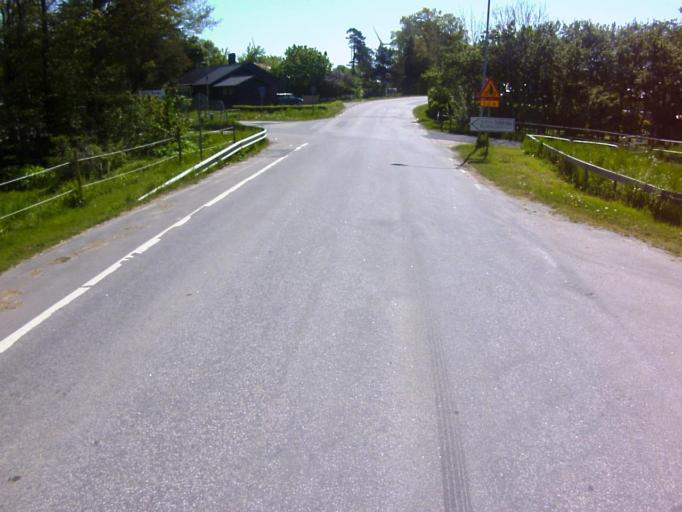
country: SE
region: Blekinge
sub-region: Solvesborgs Kommun
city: Soelvesborg
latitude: 56.0568
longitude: 14.6227
